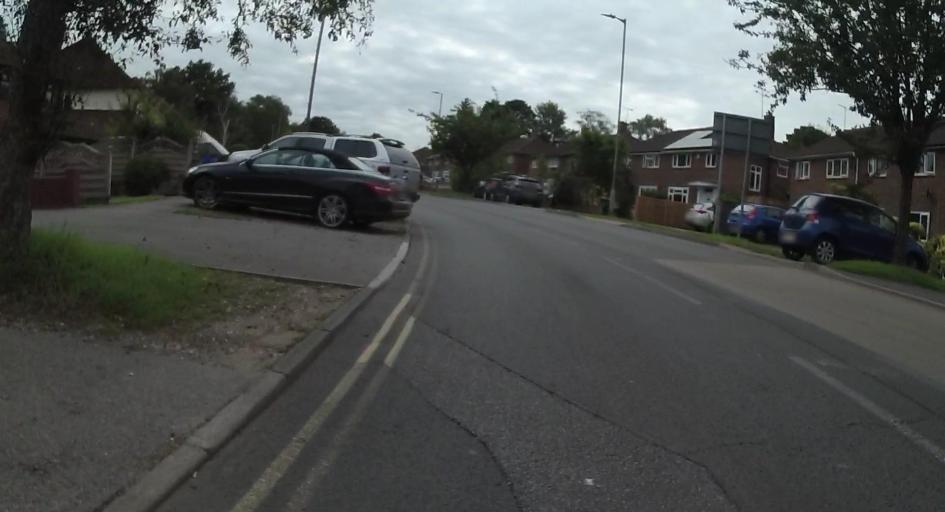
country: GB
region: England
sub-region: Surrey
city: West Byfleet
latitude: 51.3343
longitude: -0.5238
